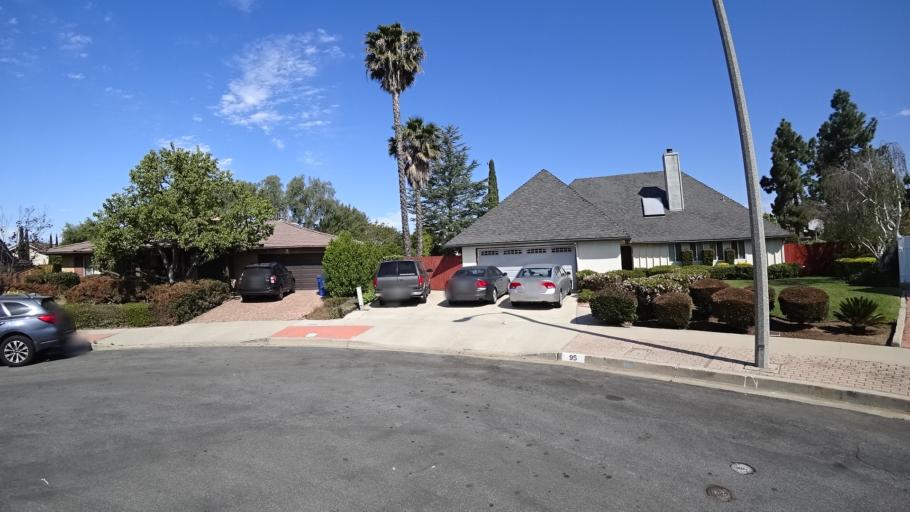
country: US
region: California
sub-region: Ventura County
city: Casa Conejo
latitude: 34.1792
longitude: -118.9266
